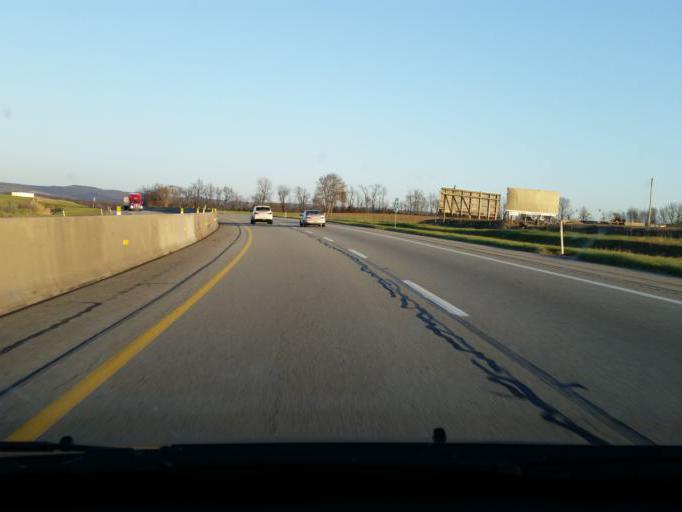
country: US
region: Pennsylvania
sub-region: Westmoreland County
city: Mount Pleasant
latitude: 40.1841
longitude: -79.5306
